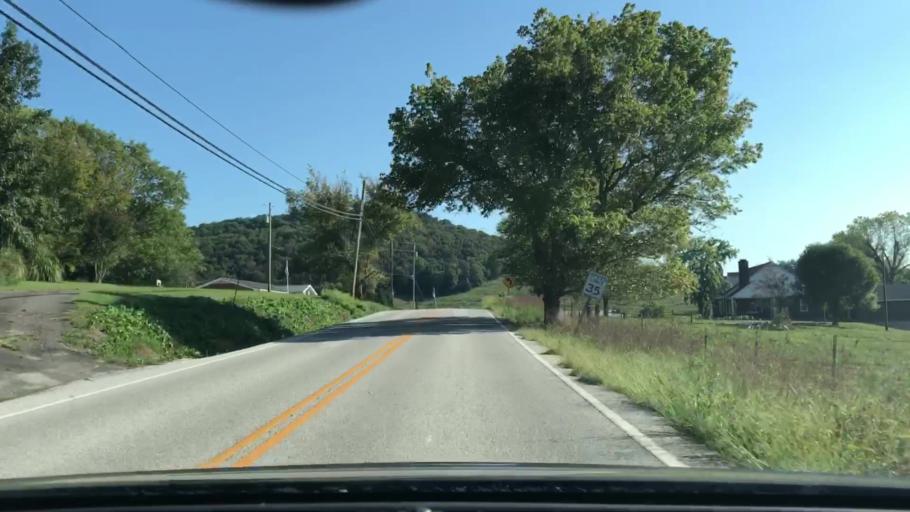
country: US
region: Tennessee
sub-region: Smith County
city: Carthage
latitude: 36.2788
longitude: -85.9486
